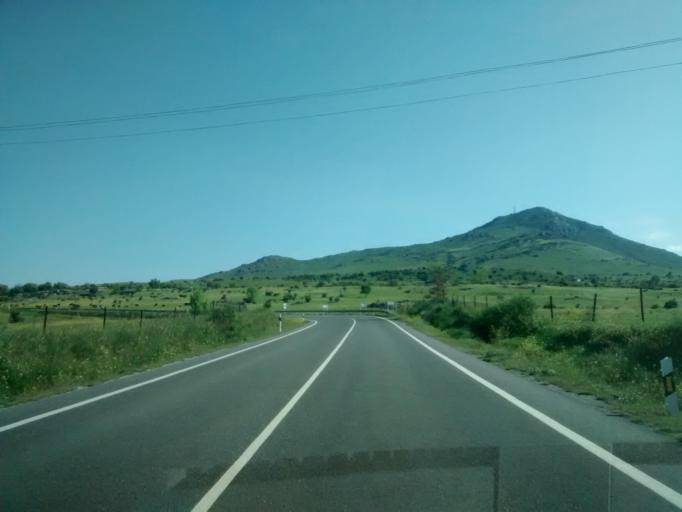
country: ES
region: Castille and Leon
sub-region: Provincia de Segovia
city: San Ildefonso
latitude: 40.9158
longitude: -4.0187
